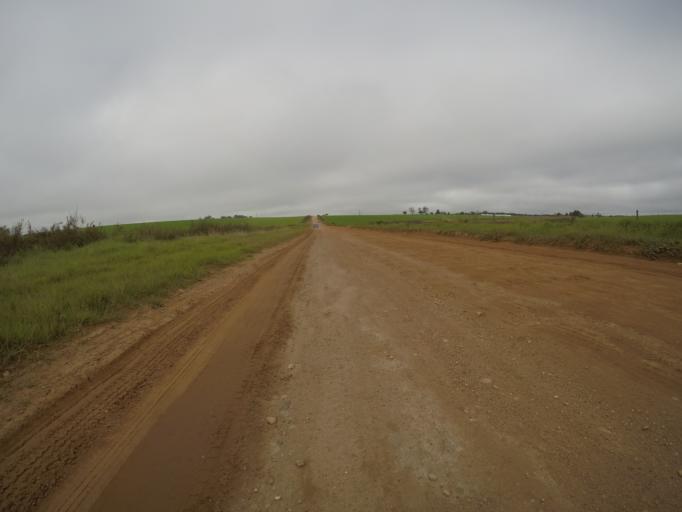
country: ZA
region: Eastern Cape
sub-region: Cacadu District Municipality
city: Kareedouw
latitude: -34.0265
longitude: 24.2421
